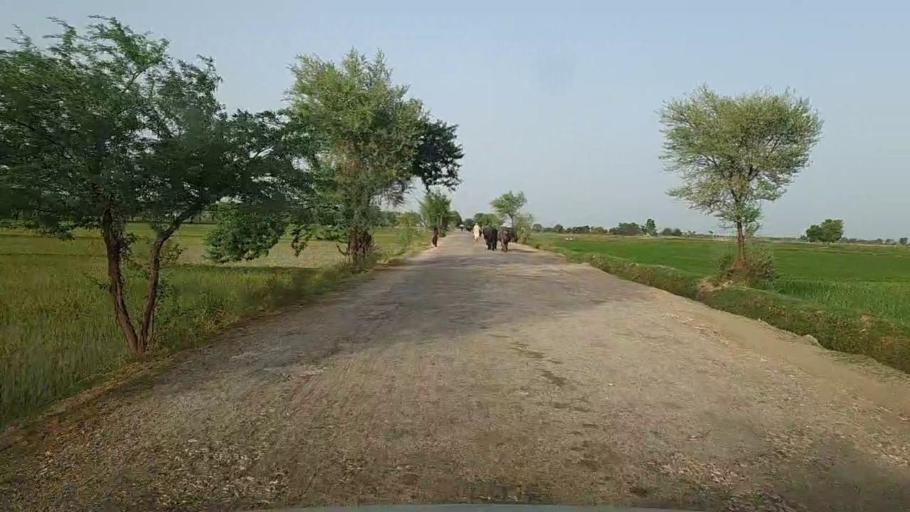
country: PK
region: Sindh
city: Mehar
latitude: 27.1600
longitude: 67.7577
